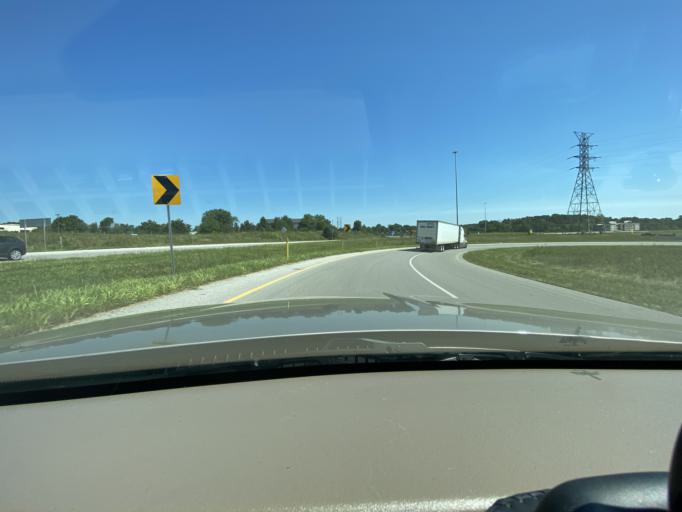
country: US
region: Indiana
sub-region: Monroe County
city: Bloomington
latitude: 39.1480
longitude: -86.5752
